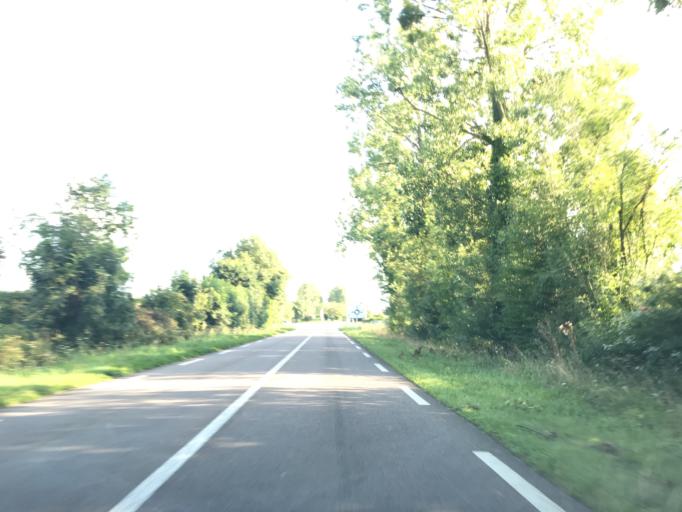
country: FR
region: Haute-Normandie
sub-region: Departement de la Seine-Maritime
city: La Remuee
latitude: 49.5309
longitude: 0.4213
